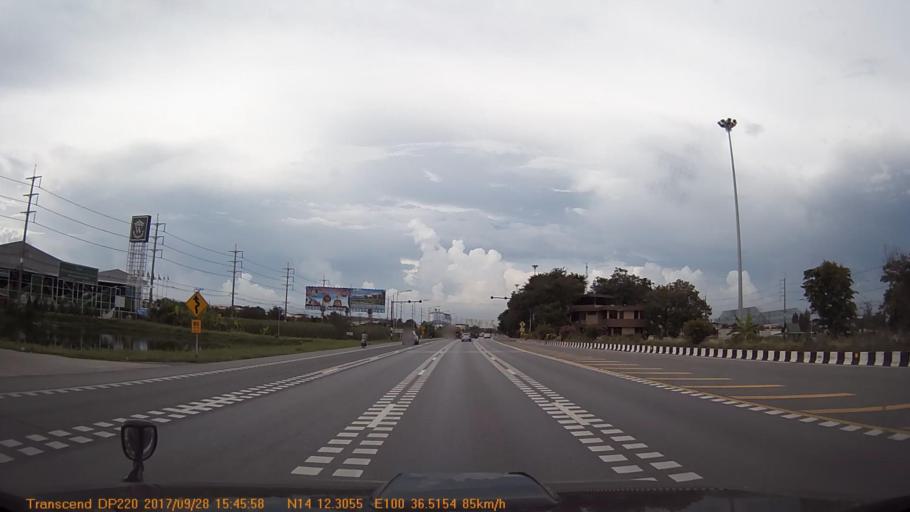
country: TH
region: Phra Nakhon Si Ayutthaya
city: Bang Pa-in
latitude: 14.2053
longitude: 100.6086
